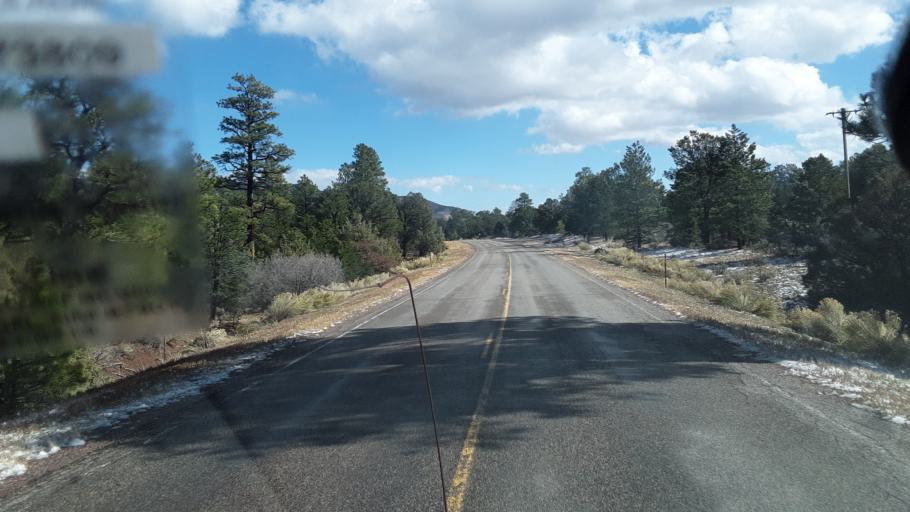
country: US
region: New Mexico
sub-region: Rio Arriba County
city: Santa Teresa
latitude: 36.2012
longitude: -106.7309
